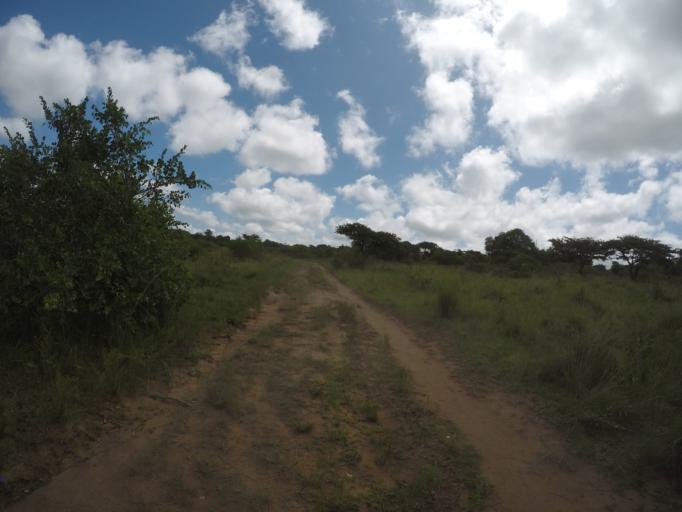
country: ZA
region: KwaZulu-Natal
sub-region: uThungulu District Municipality
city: Empangeni
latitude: -28.5867
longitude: 31.8351
